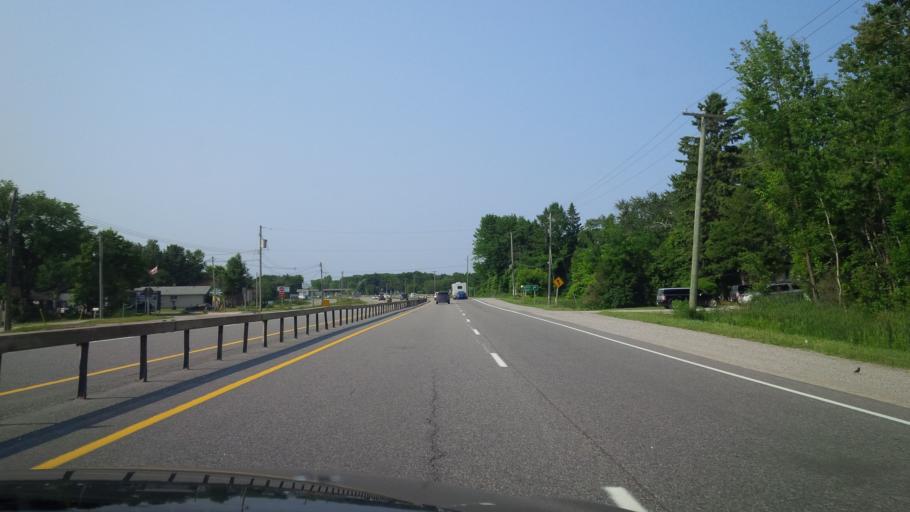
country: CA
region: Ontario
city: Orillia
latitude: 44.6763
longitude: -79.4079
